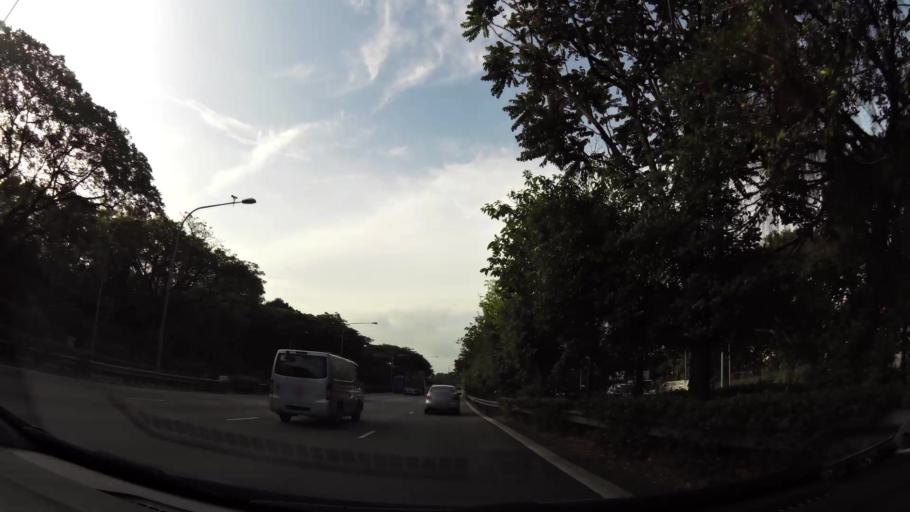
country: MY
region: Johor
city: Johor Bahru
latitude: 1.3329
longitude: 103.6759
